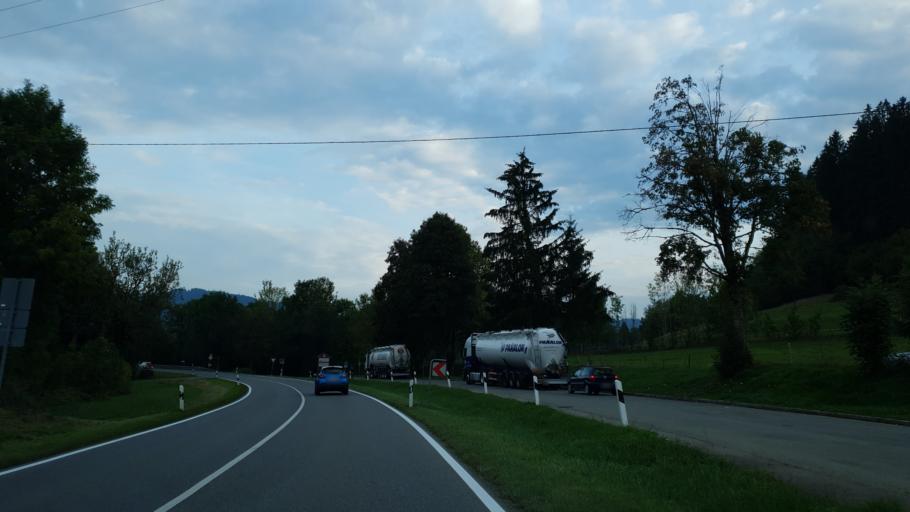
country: DE
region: Baden-Wuerttemberg
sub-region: Tuebingen Region
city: Isny im Allgau
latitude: 47.6832
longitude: 10.0786
